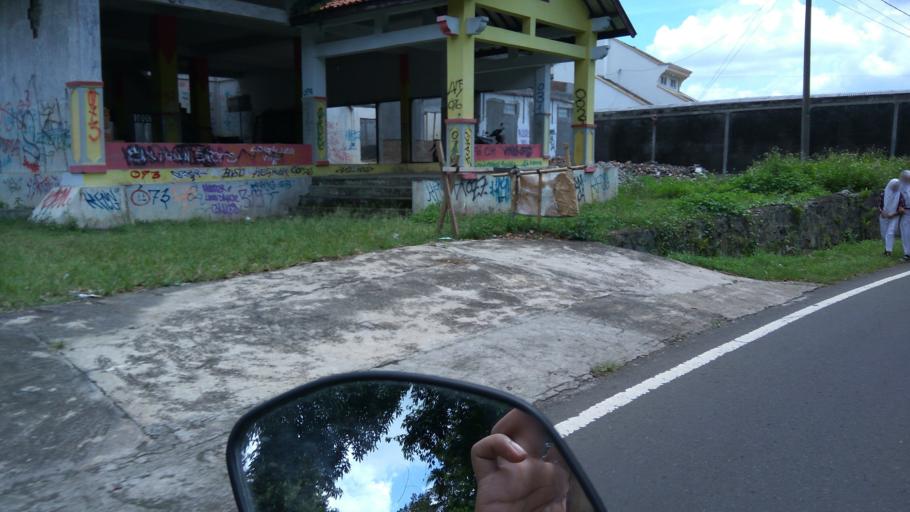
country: ID
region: Central Java
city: Ambarawa
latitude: -7.2436
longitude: 110.3938
